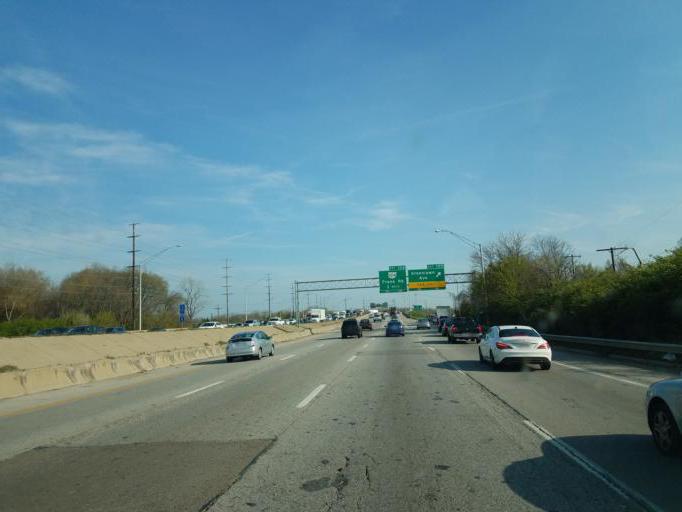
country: US
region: Ohio
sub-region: Franklin County
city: Columbus
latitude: 39.9425
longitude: -83.0119
